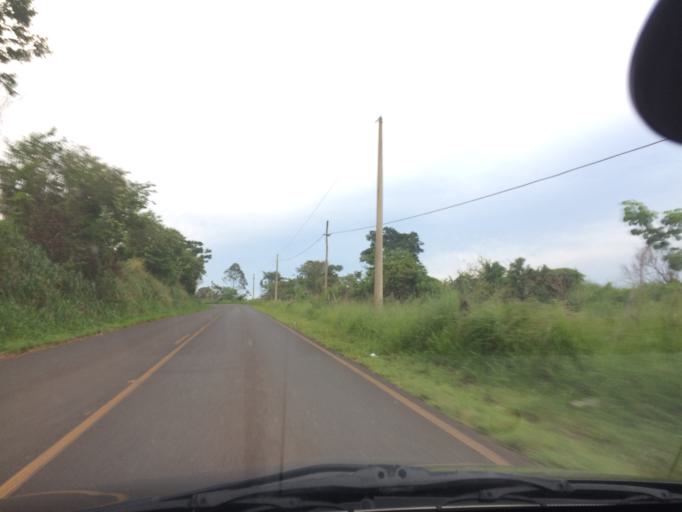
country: BR
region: Sao Paulo
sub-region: Casa Branca
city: Casa Branca
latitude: -21.7621
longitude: -47.1062
